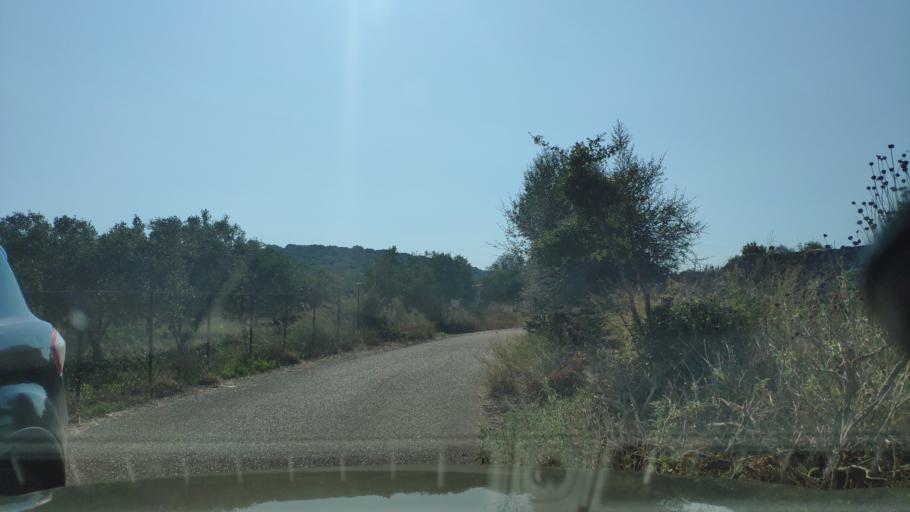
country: GR
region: West Greece
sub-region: Nomos Aitolias kai Akarnanias
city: Amfilochia
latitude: 38.9052
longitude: 21.1097
